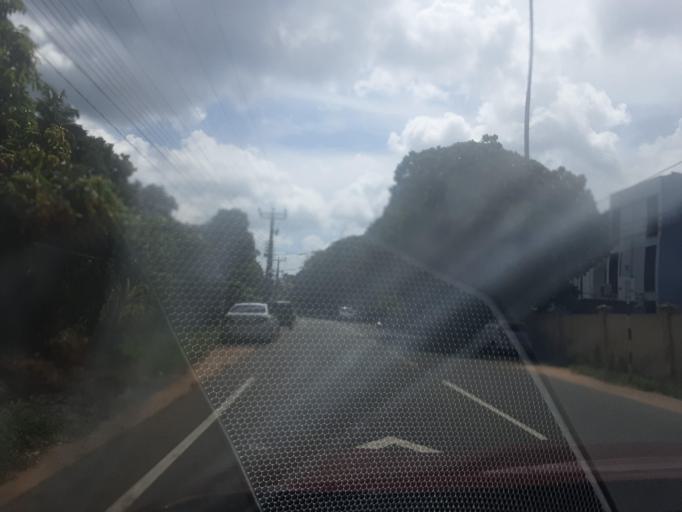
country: LK
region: North Western
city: Kuliyapitiya
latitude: 7.4699
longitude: 80.0491
